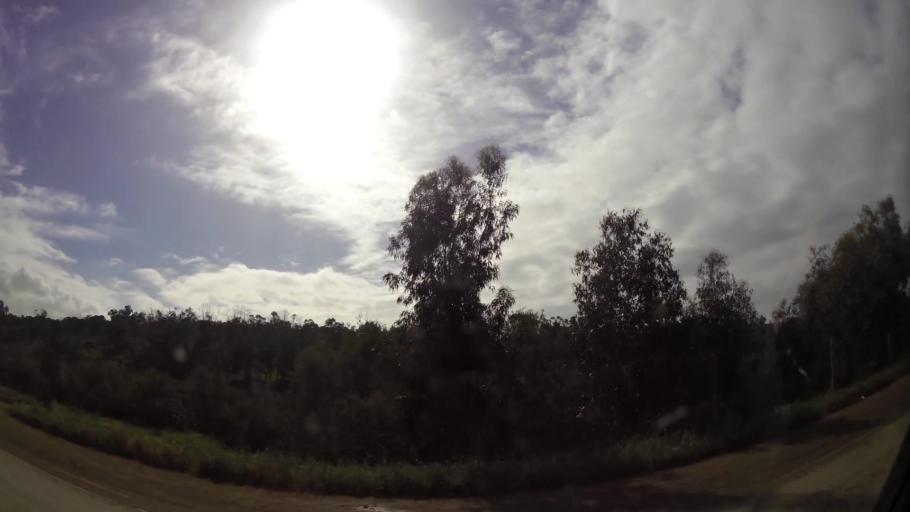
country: MA
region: Grand Casablanca
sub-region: Mohammedia
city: Mohammedia
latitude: 33.6635
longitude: -7.3992
